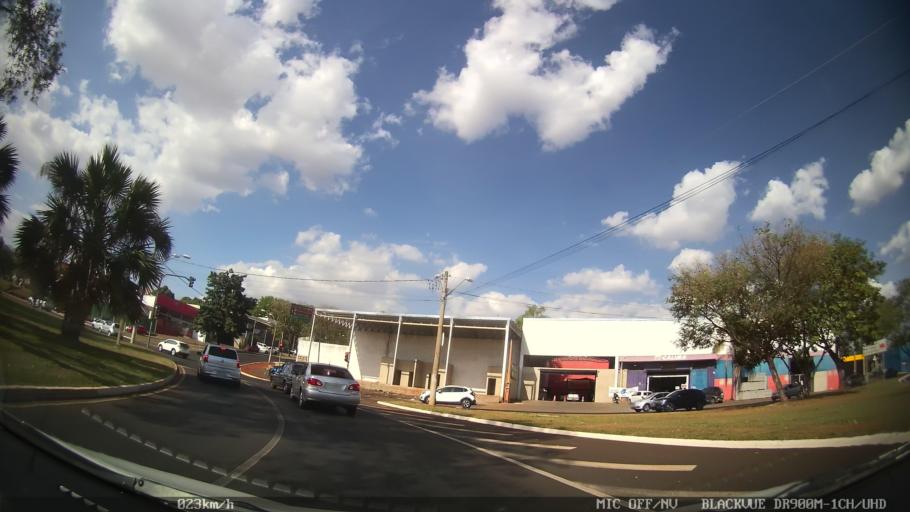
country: BR
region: Sao Paulo
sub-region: Ribeirao Preto
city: Ribeirao Preto
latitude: -21.1954
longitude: -47.8225
